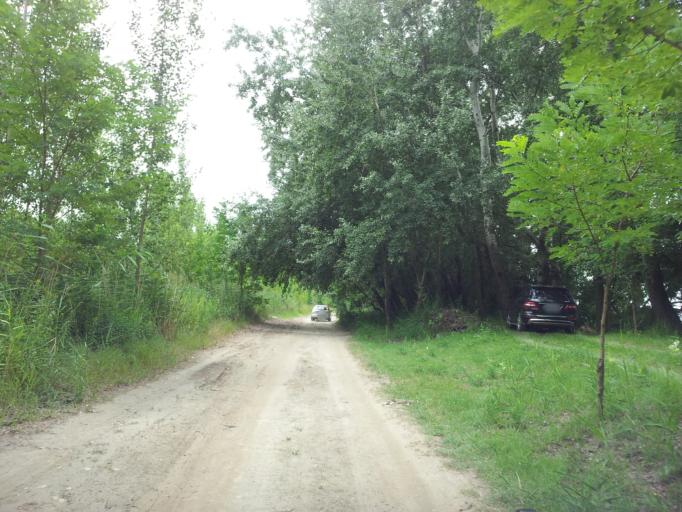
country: HU
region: Pest
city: Szigetcsep
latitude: 47.2267
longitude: 18.9707
